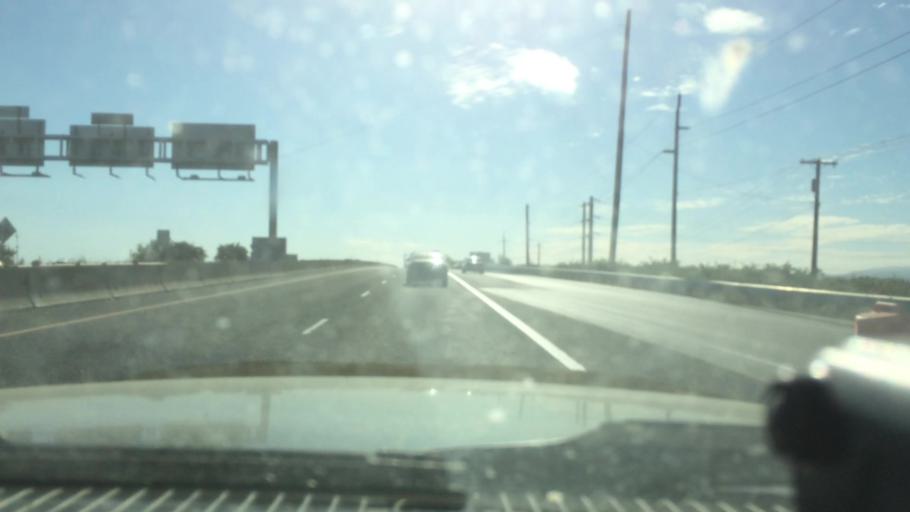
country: US
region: Oregon
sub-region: Lane County
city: Eugene
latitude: 44.0980
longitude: -123.1537
